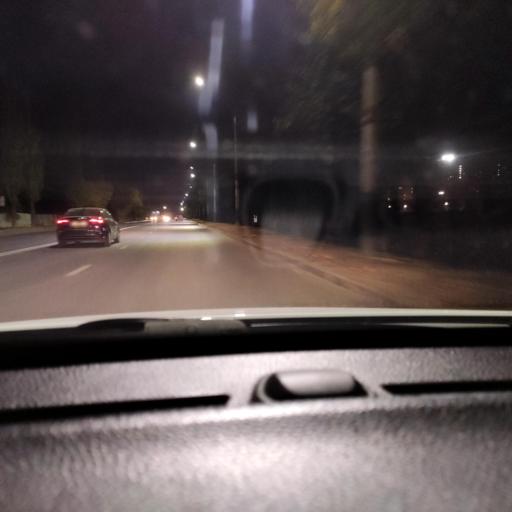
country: RU
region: Voronezj
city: Somovo
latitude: 51.7120
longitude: 39.2756
